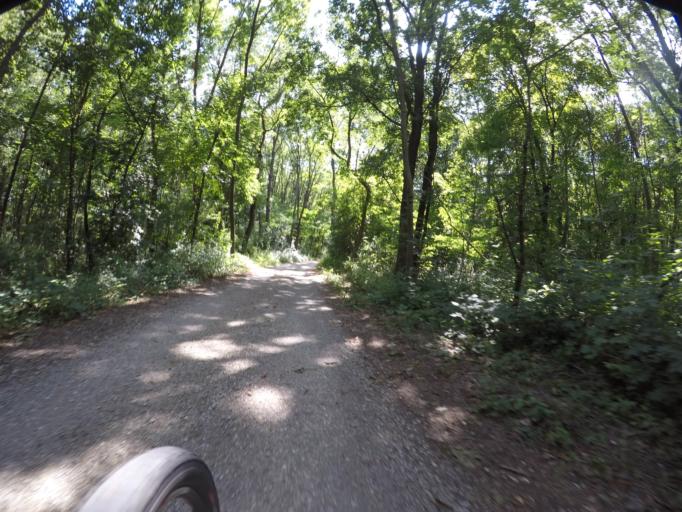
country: AT
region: Lower Austria
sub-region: Politischer Bezirk Ganserndorf
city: Gross-Enzersdorf
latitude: 48.1836
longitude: 16.5360
